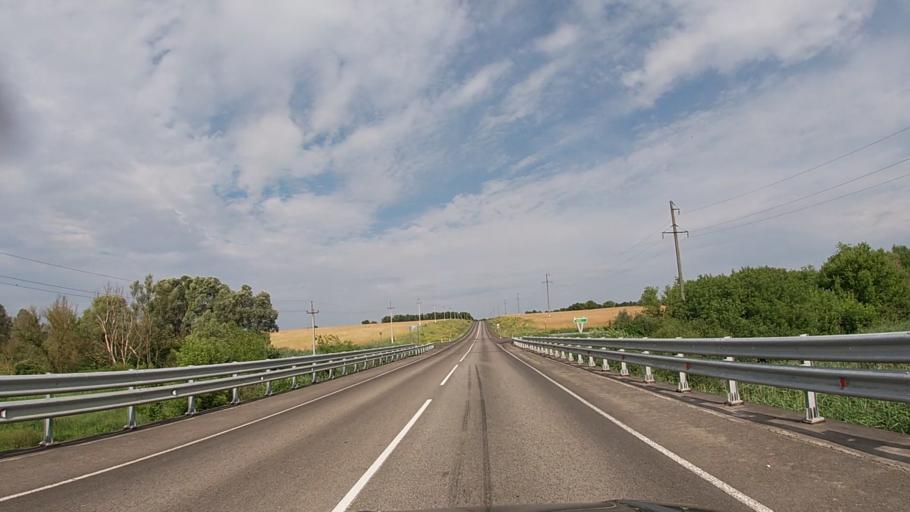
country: RU
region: Belgorod
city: Krasnaya Yaruga
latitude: 50.7997
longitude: 35.5703
